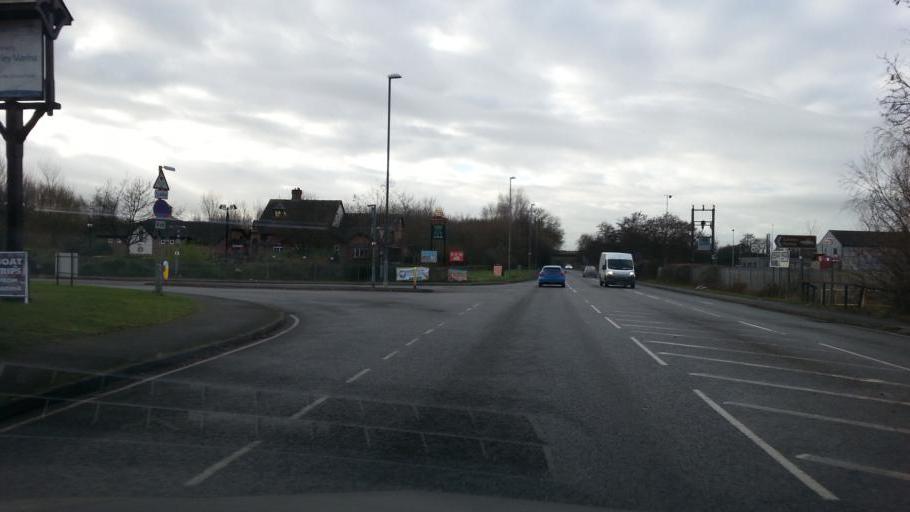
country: GB
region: England
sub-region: Derbyshire
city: Long Eaton
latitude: 52.8724
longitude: -1.3035
